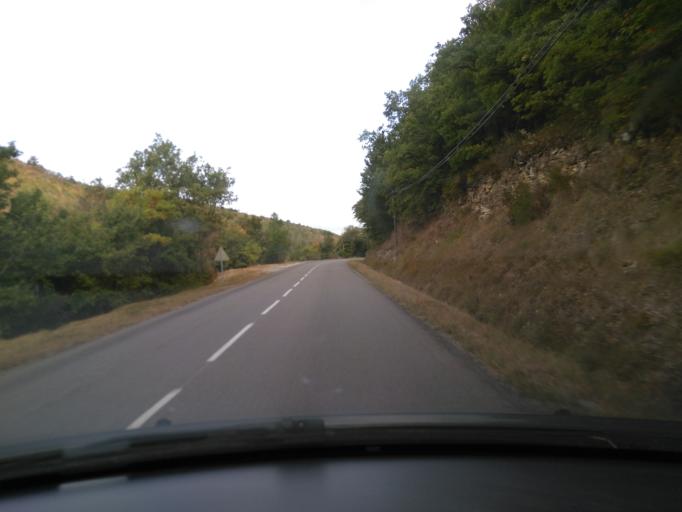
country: FR
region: Rhone-Alpes
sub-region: Departement de la Drome
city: La Begude-de-Mazenc
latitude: 44.5103
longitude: 4.9379
